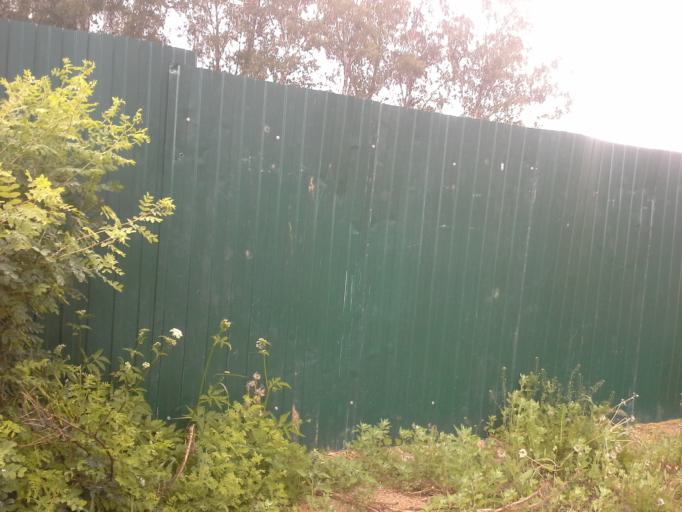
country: RU
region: Moskovskaya
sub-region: Leninskiy Rayon
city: Vnukovo
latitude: 55.6235
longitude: 37.2861
